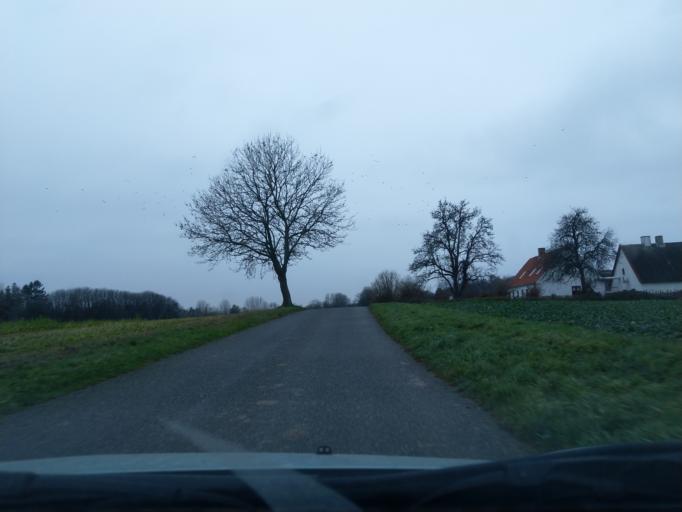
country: DK
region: Zealand
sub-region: Vordingborg Kommune
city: Praesto
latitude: 55.1140
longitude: 12.1534
